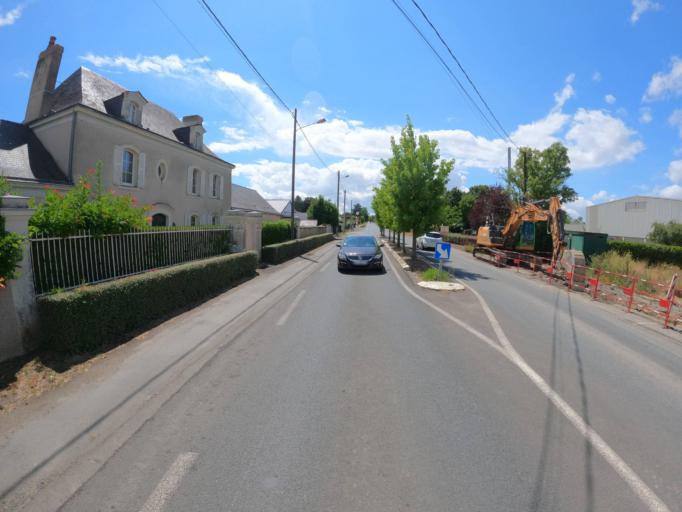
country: FR
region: Pays de la Loire
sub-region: Departement de Maine-et-Loire
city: Champigne
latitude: 47.6600
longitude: -0.5739
